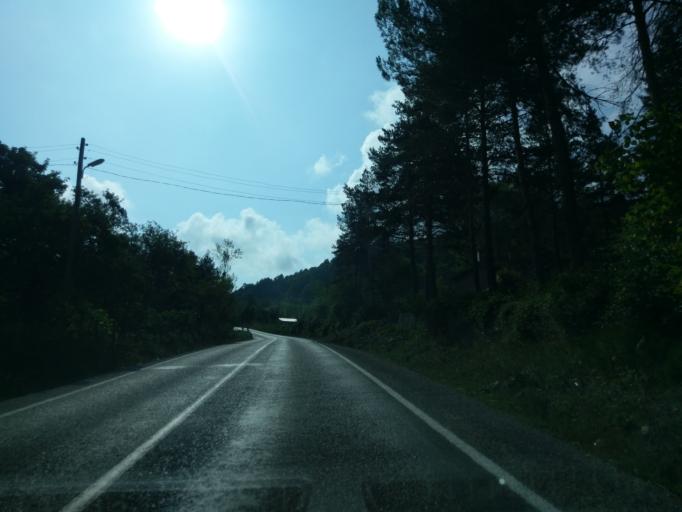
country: TR
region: Sinop
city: Ayancik
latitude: 41.8794
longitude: 34.5070
